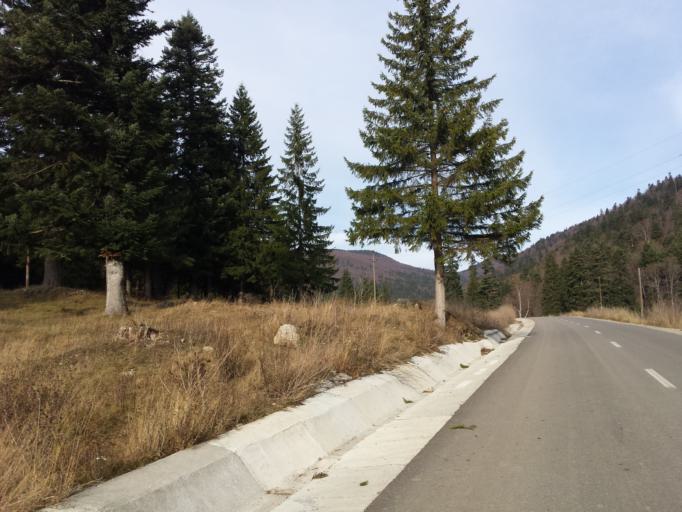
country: RO
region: Prahova
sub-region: Oras Azuga
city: Azuga
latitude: 45.4366
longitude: 25.5293
